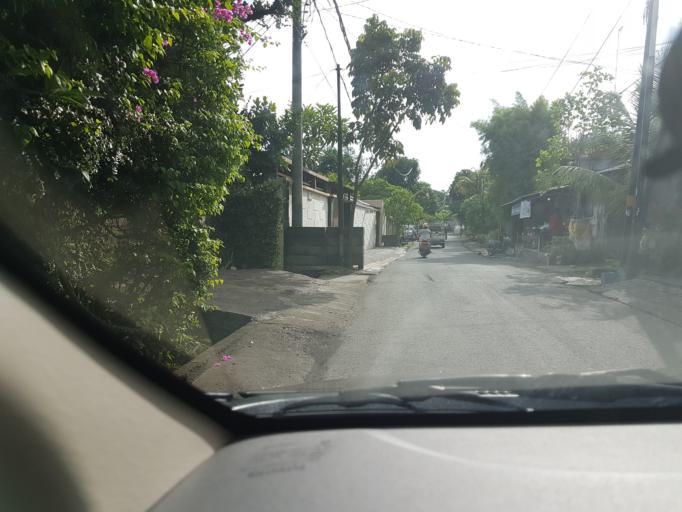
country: ID
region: Bali
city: Kuta
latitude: -8.6831
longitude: 115.1748
